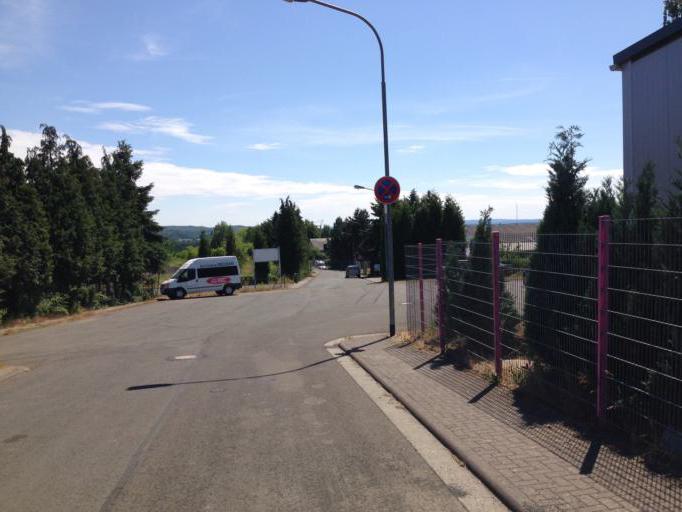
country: DE
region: Hesse
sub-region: Regierungsbezirk Giessen
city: Alten Buseck
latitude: 50.6185
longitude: 8.7379
